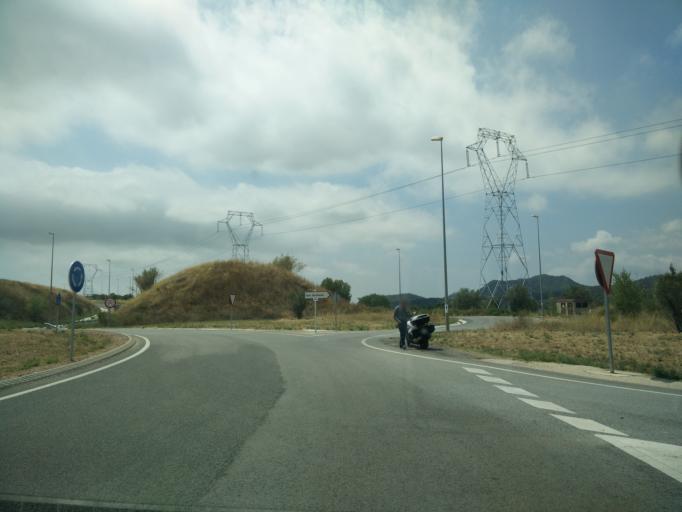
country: ES
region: Catalonia
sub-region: Provincia de Barcelona
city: Terrassa
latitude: 41.5840
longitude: 1.9923
